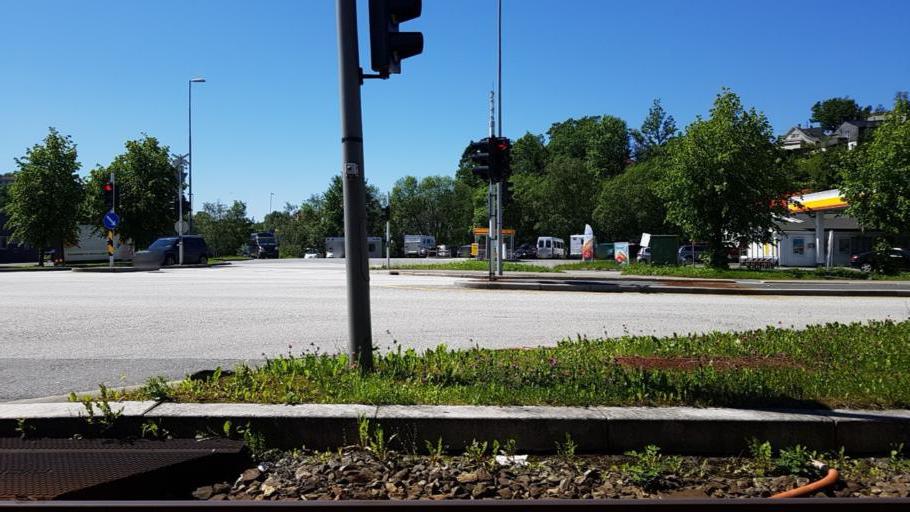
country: NO
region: Hordaland
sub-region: Bergen
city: Sandsli
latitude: 60.3207
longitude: 5.3519
